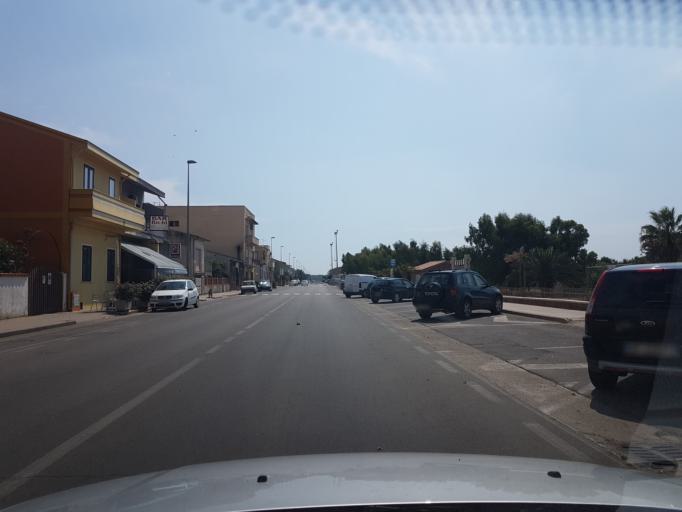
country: IT
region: Sardinia
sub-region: Provincia di Oristano
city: Cabras
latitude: 39.9249
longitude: 8.5262
